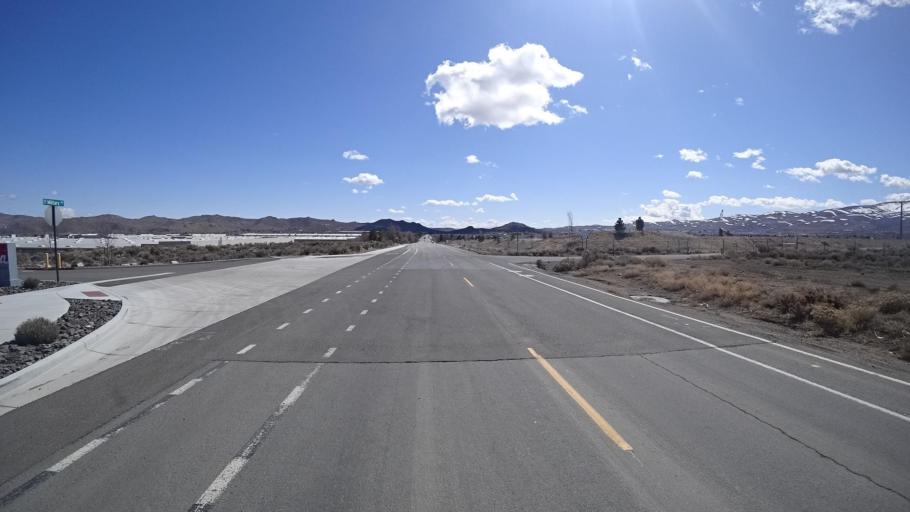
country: US
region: Nevada
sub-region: Washoe County
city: Lemmon Valley
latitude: 39.6472
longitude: -119.8670
